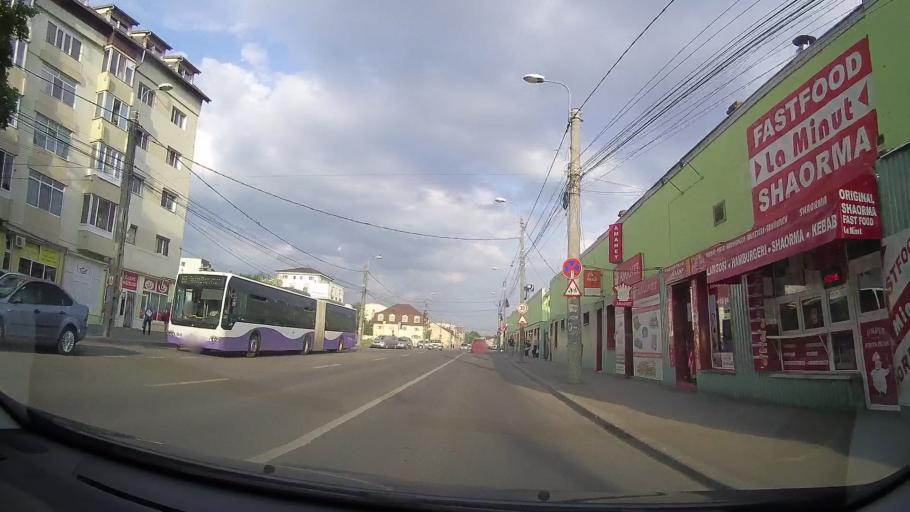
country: RO
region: Timis
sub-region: Comuna Dumbravita
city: Dumbravita
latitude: 45.7754
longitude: 21.2381
